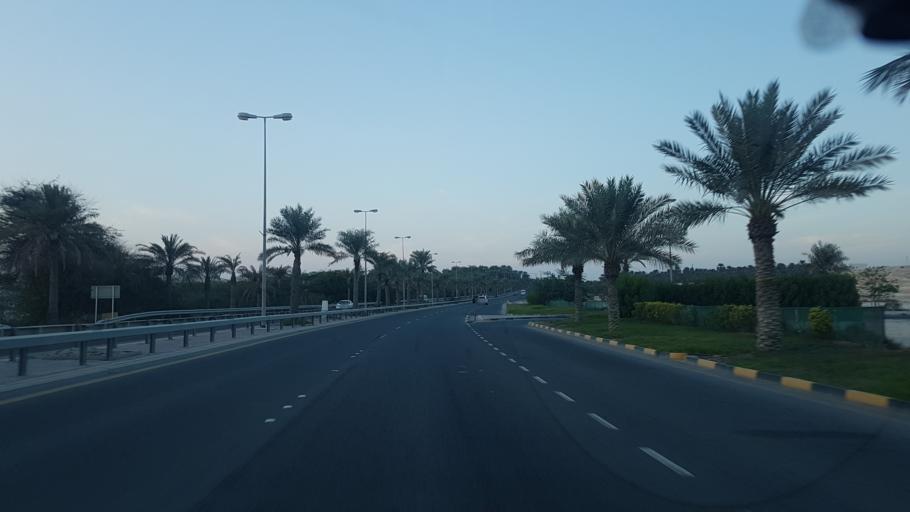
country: BH
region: Northern
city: Ar Rifa'
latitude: 26.1125
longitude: 50.5378
